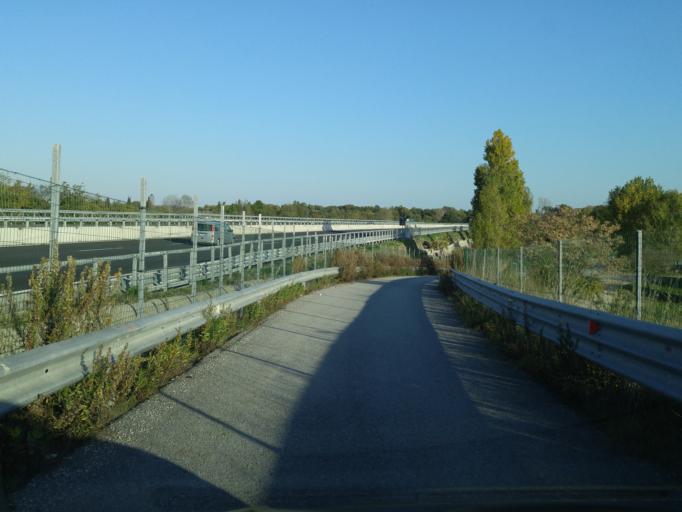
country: IT
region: The Marches
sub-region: Provincia di Pesaro e Urbino
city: Fano
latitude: 43.8131
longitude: 13.0319
